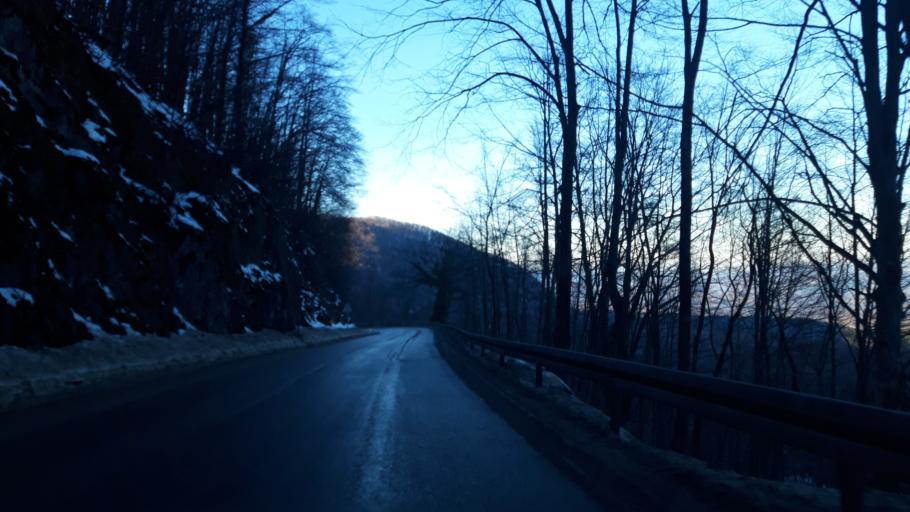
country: BA
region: Republika Srpska
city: Vlasenica
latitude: 44.1572
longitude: 18.9280
